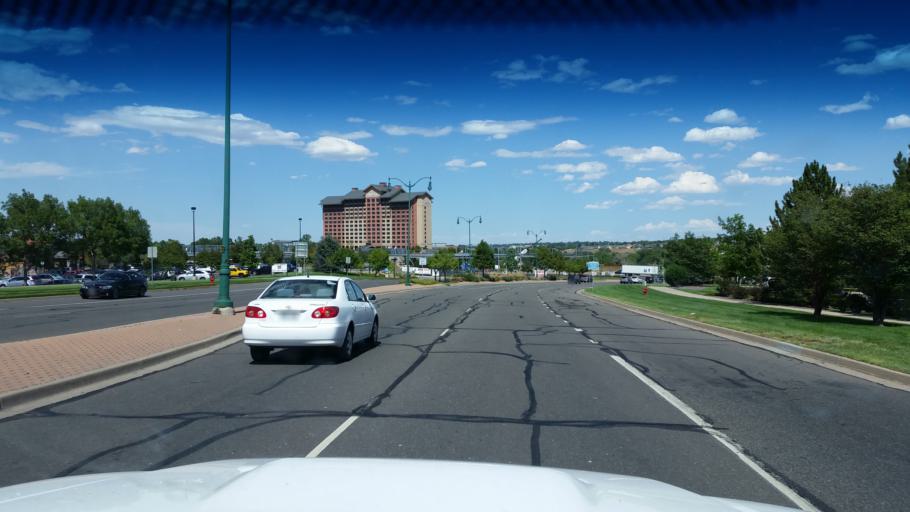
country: US
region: Colorado
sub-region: Broomfield County
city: Broomfield
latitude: 39.8874
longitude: -105.0706
